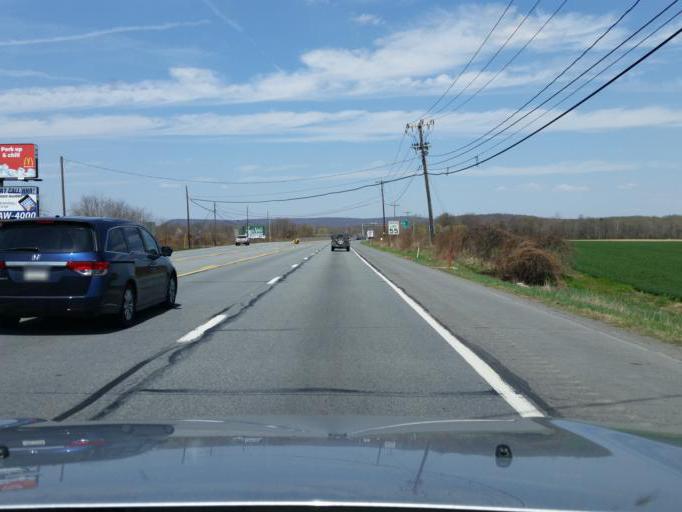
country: US
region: Pennsylvania
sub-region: Perry County
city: Duncannon
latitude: 40.4132
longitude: -77.0116
